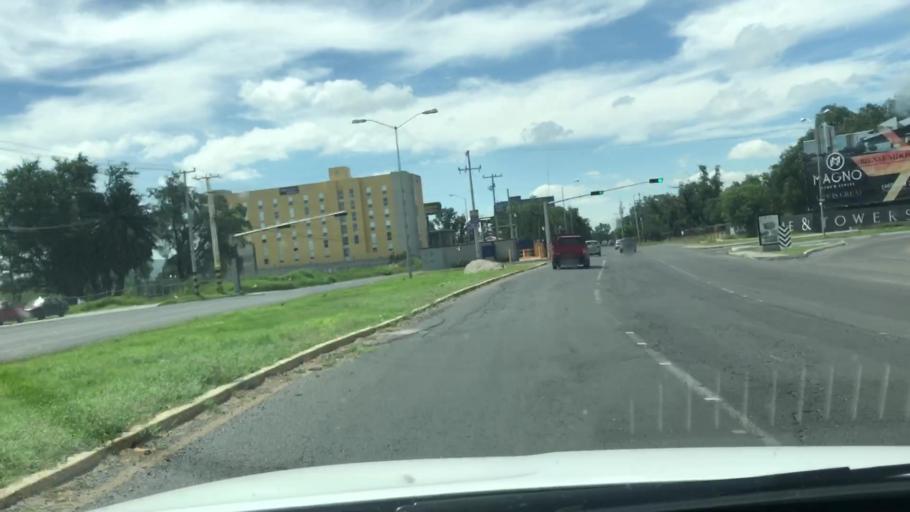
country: MX
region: Guanajuato
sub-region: Celaya
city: La Trinidad
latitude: 20.5309
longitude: -100.7765
